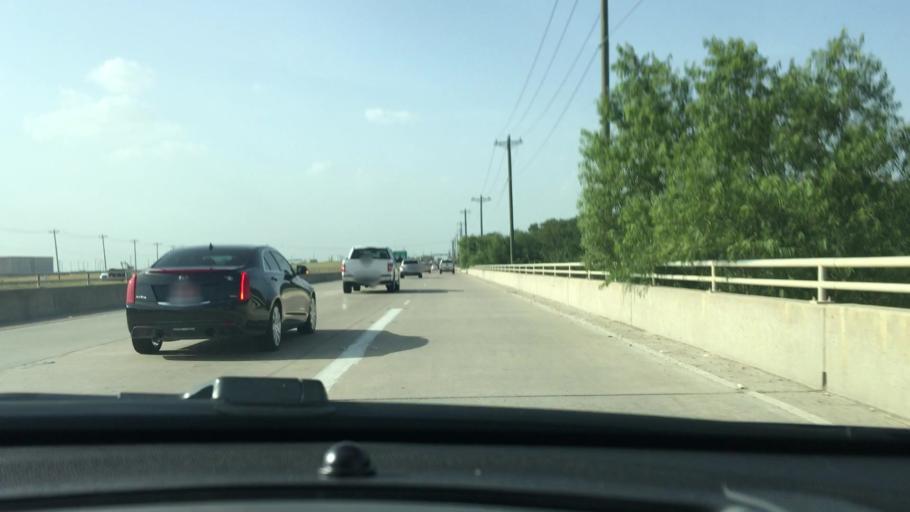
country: US
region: Texas
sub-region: Collin County
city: Prosper
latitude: 33.2133
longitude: -96.8200
